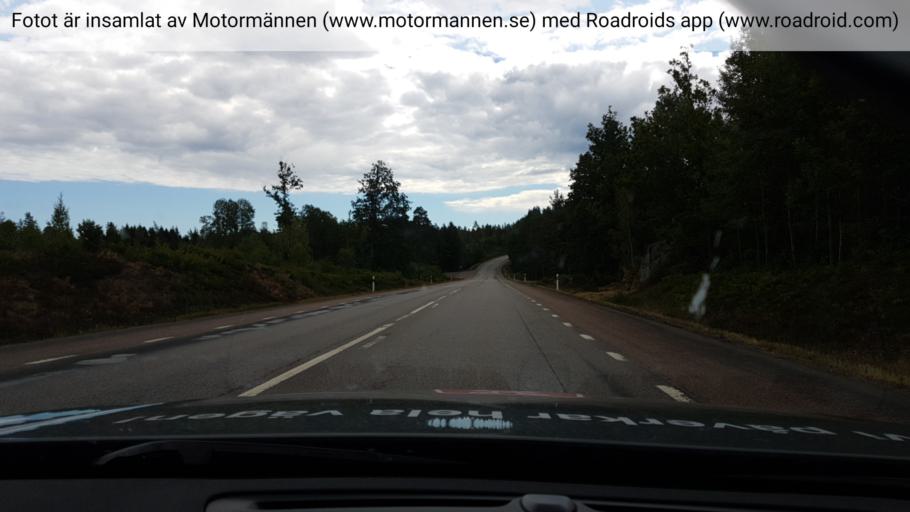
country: SE
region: Kalmar
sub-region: Vasterviks Kommun
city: Ankarsrum
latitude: 57.6333
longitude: 16.4552
